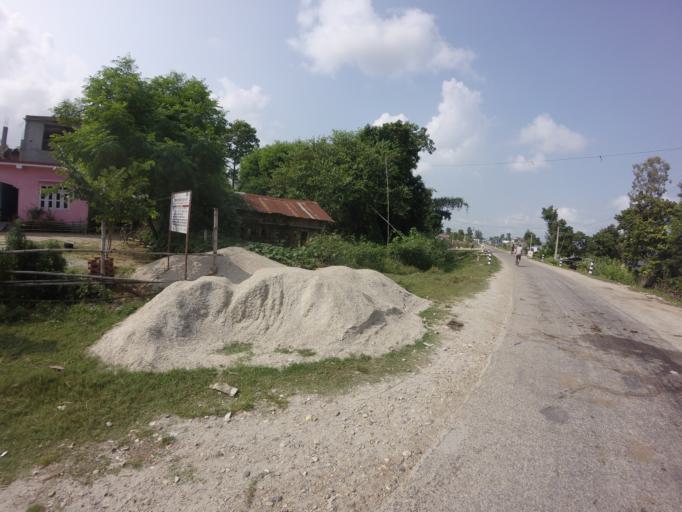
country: NP
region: Far Western
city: Tikapur
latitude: 28.4566
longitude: 81.0765
